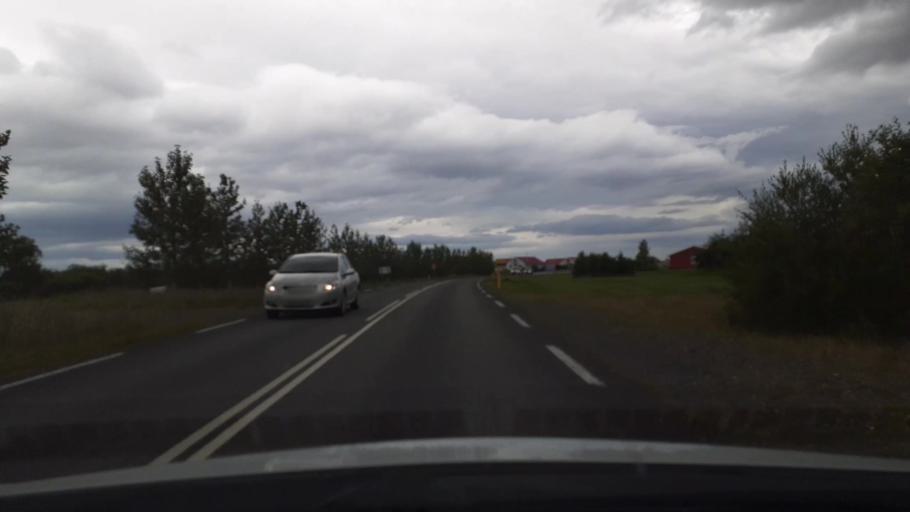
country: IS
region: West
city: Borgarnes
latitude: 64.5600
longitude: -21.7574
